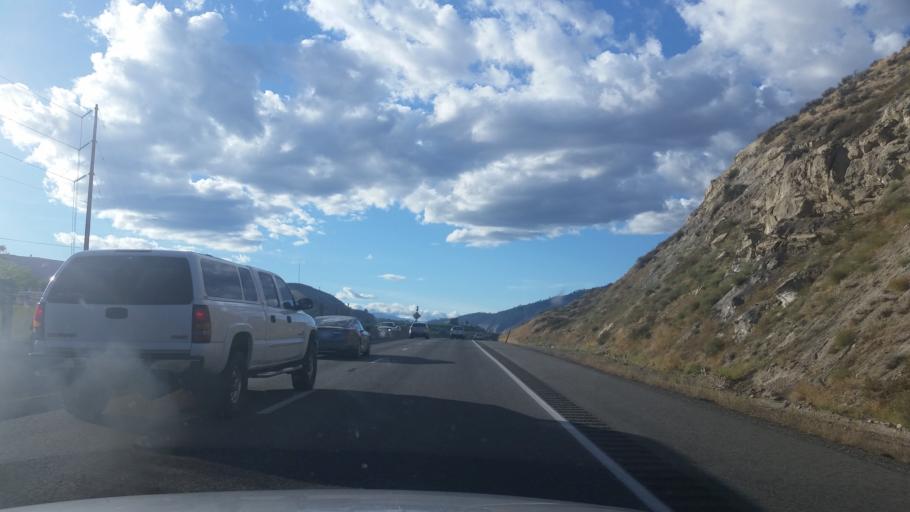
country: US
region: Washington
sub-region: Chelan County
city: Cashmere
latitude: 47.4902
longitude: -120.4167
